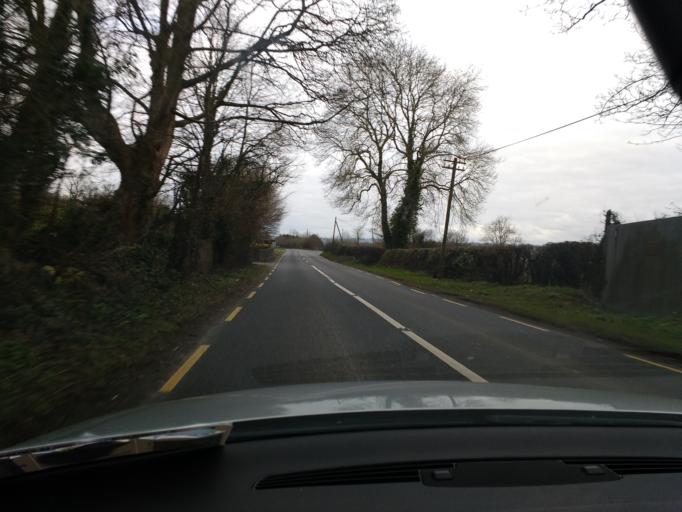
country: IE
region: Leinster
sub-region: Kilkenny
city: Kilkenny
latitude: 52.6854
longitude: -7.2752
